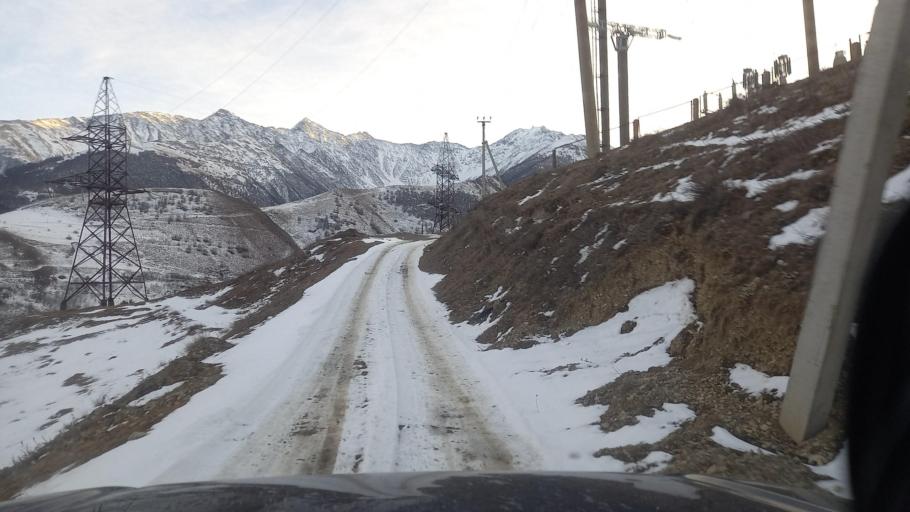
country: RU
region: Ingushetiya
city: Dzhayrakh
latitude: 42.8460
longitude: 44.5135
